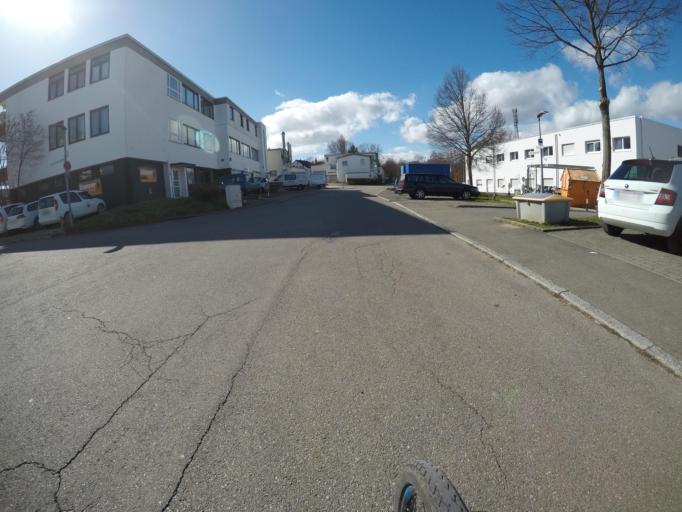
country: DE
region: Baden-Wuerttemberg
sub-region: Regierungsbezirk Stuttgart
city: Steinenbronn
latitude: 48.7070
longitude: 9.1273
